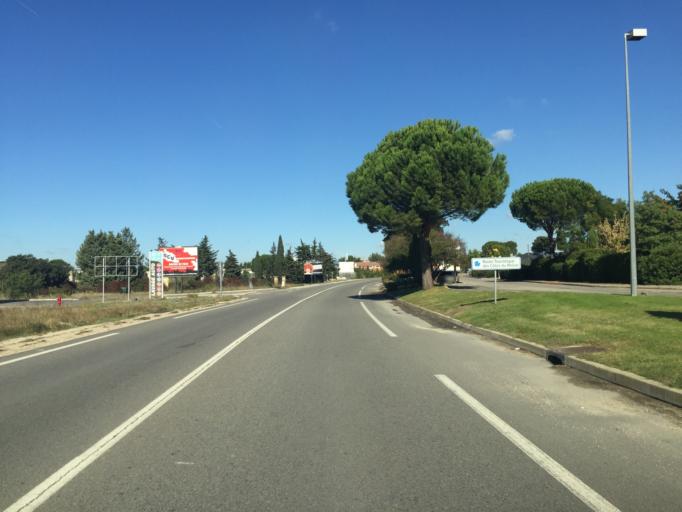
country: FR
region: Provence-Alpes-Cote d'Azur
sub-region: Departement du Vaucluse
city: Morieres-les-Avignon
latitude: 43.9584
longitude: 4.8997
